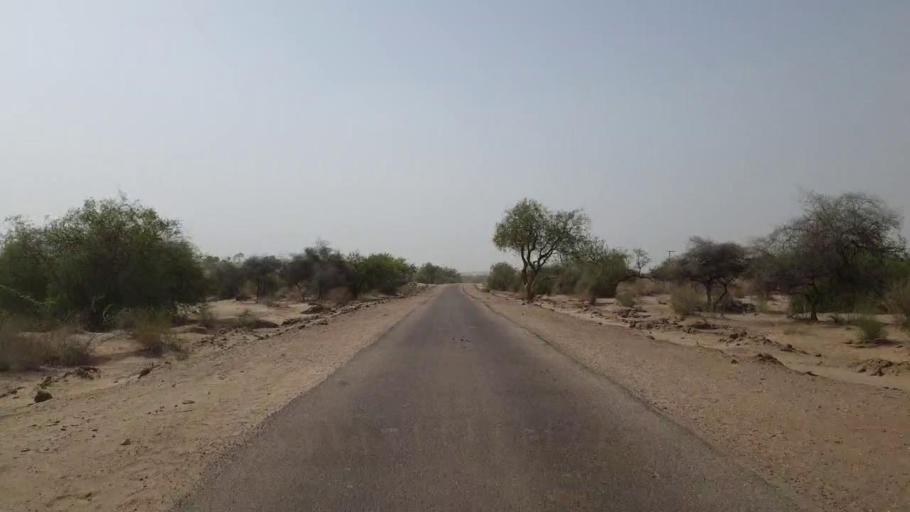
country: PK
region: Sindh
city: Mithi
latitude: 24.6037
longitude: 69.9224
